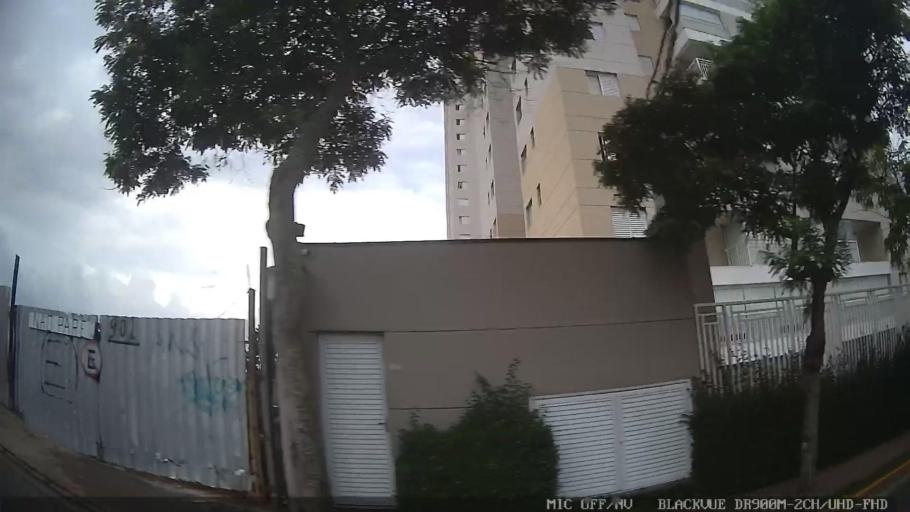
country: BR
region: Sao Paulo
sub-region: Mogi das Cruzes
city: Mogi das Cruzes
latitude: -23.5422
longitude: -46.1982
